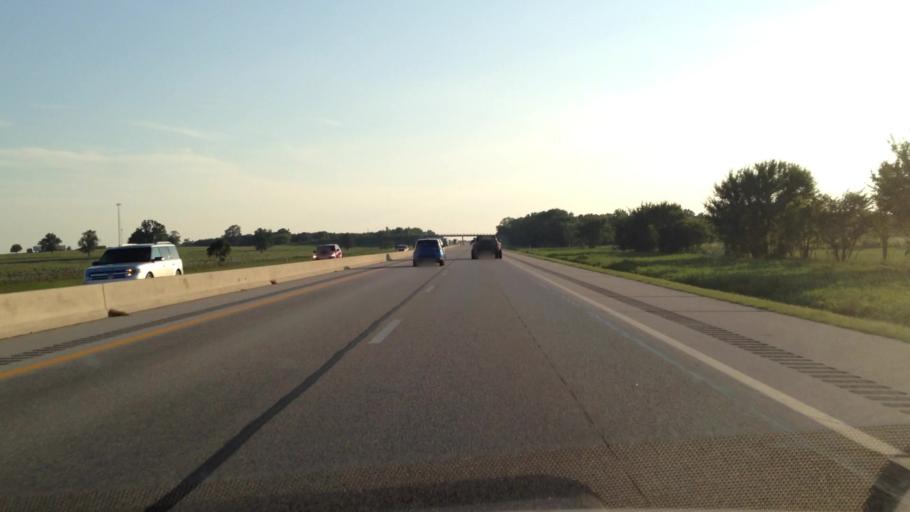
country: US
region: Kansas
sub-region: Cherokee County
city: Baxter Springs
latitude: 36.9532
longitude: -94.6724
